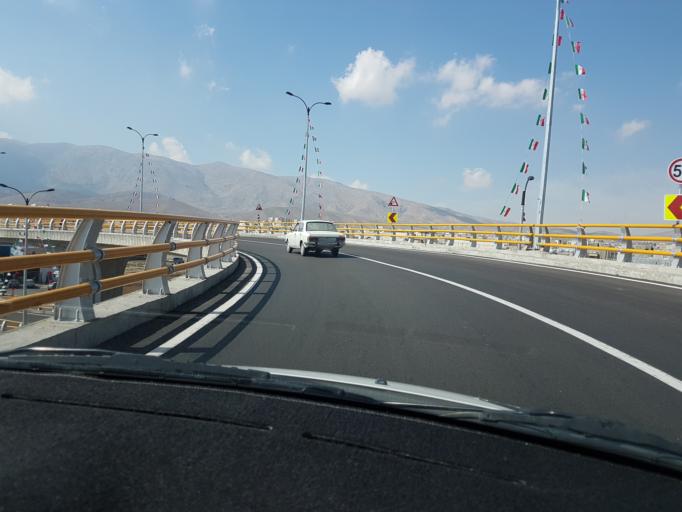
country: IR
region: Fars
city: Shiraz
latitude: 29.6115
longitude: 52.4685
